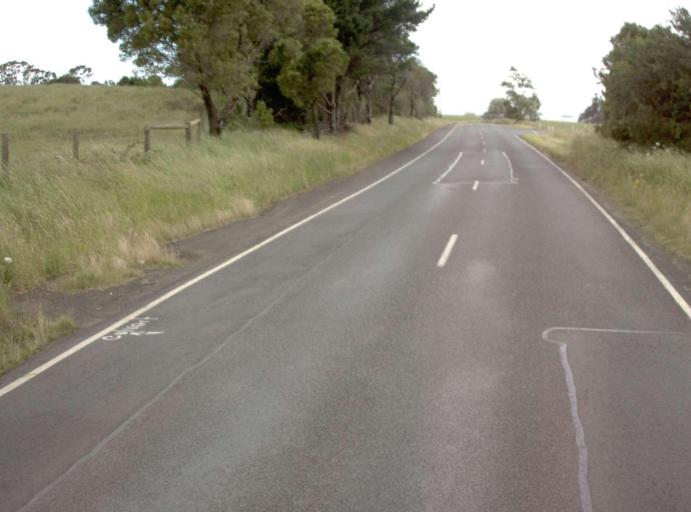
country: AU
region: Victoria
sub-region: Baw Baw
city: Warragul
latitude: -38.1312
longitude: 145.9304
